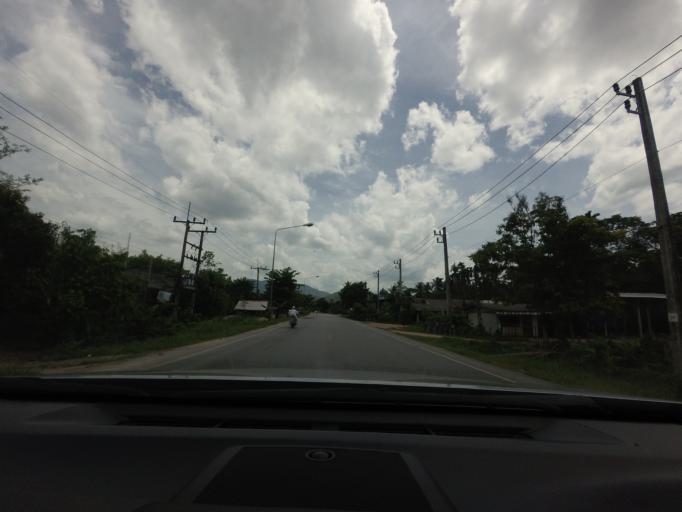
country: TH
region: Yala
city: Raman
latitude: 6.4600
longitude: 101.3674
